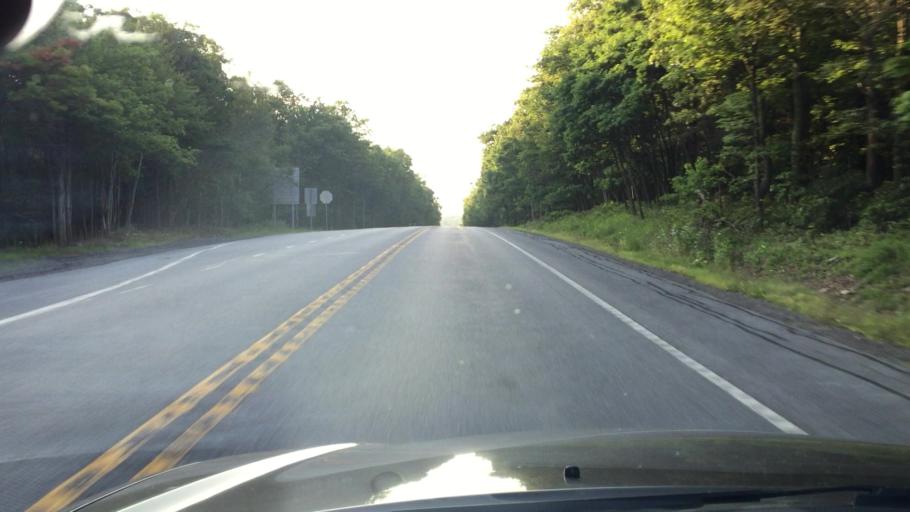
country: US
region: Pennsylvania
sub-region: Carbon County
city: Nesquehoning
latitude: 40.8882
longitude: -75.8030
